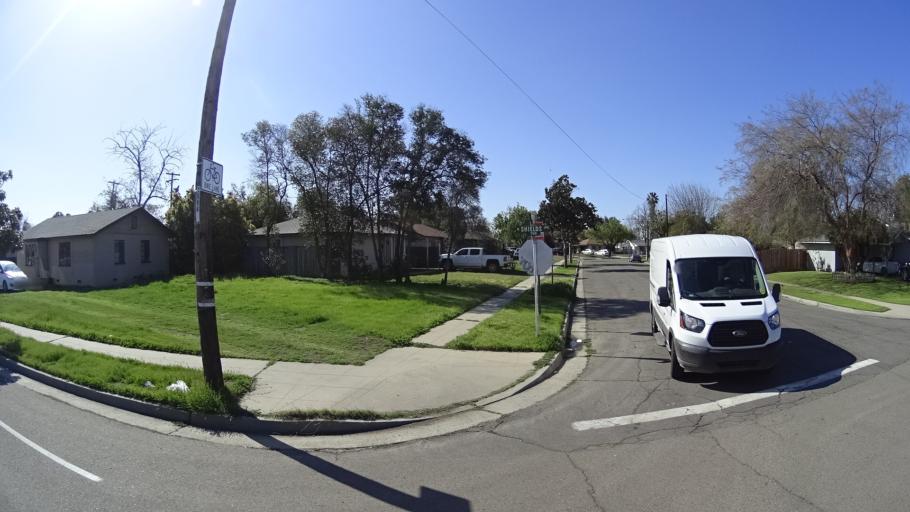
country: US
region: California
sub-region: Fresno County
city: Fresno
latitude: 36.7793
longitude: -119.8207
